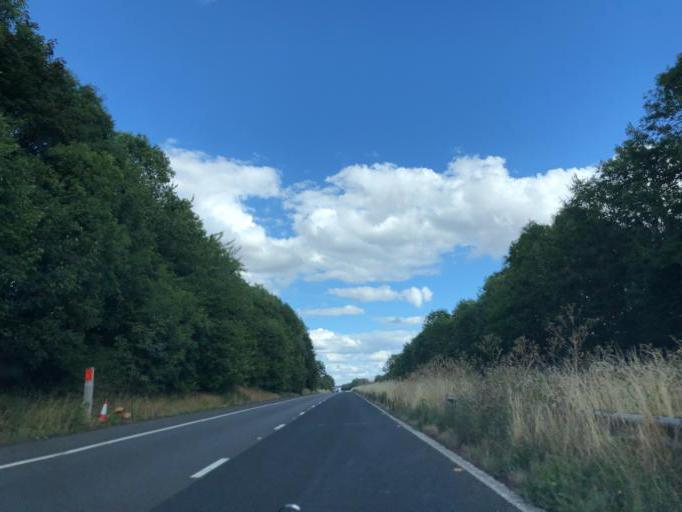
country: GB
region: England
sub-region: Northamptonshire
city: Daventry
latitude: 52.3298
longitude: -1.1734
